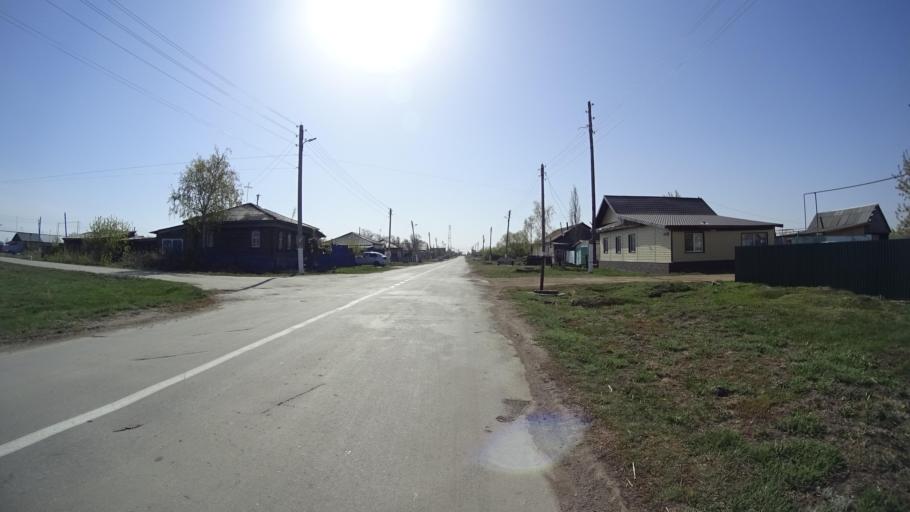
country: RU
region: Chelyabinsk
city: Chesma
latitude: 53.7973
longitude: 61.0266
